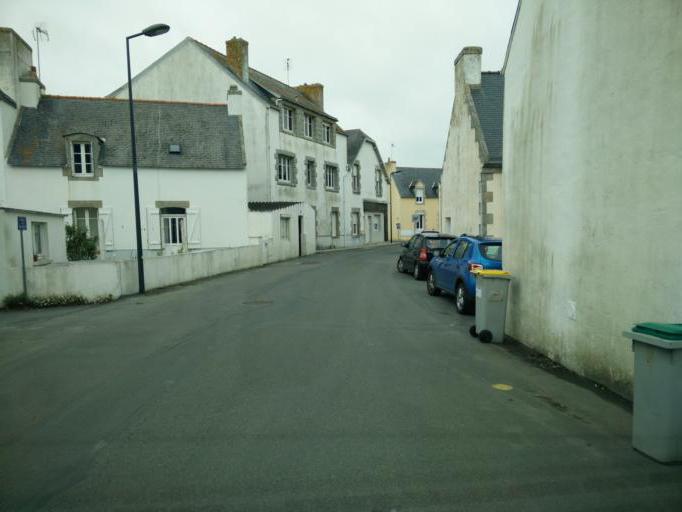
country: FR
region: Brittany
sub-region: Departement du Finistere
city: Plobannalec-Lesconil
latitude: 47.7957
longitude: -4.2168
